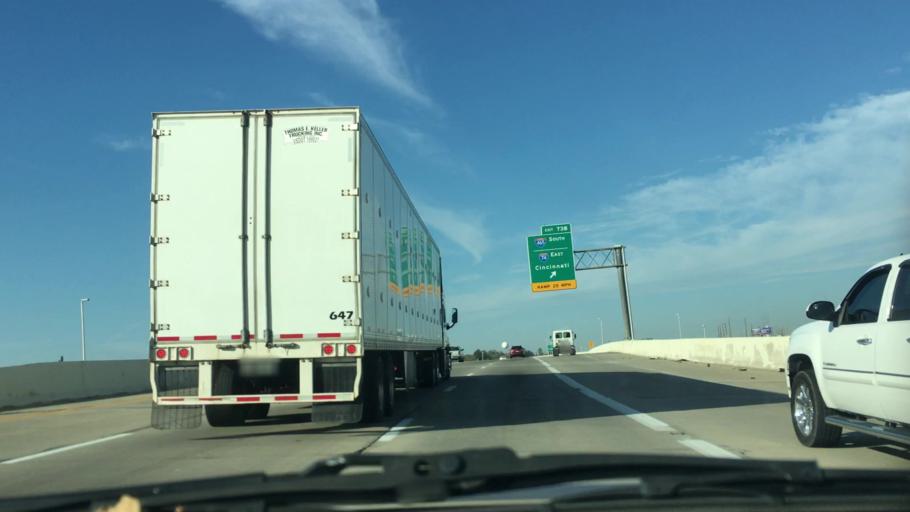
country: US
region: Indiana
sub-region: Marion County
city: Speedway
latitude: 39.7135
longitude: -86.2628
